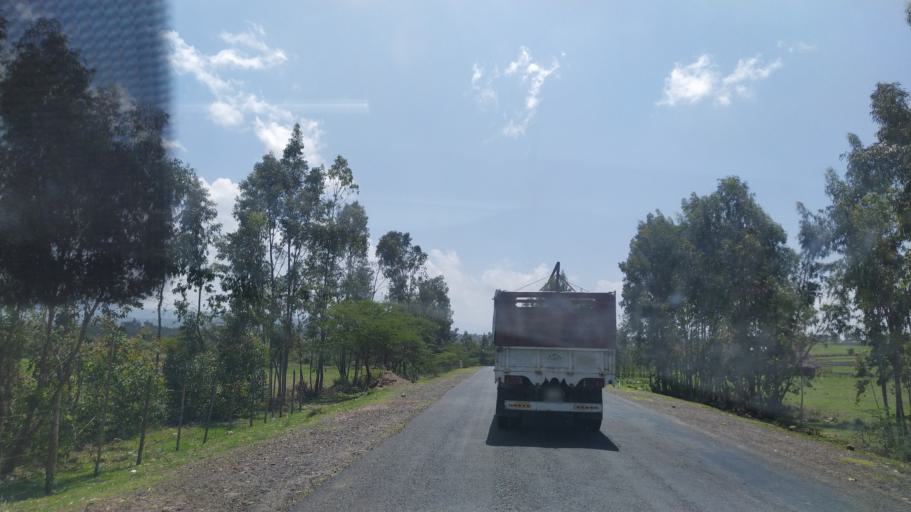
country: ET
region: Southern Nations, Nationalities, and People's Region
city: Butajira
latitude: 7.7711
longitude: 38.1386
